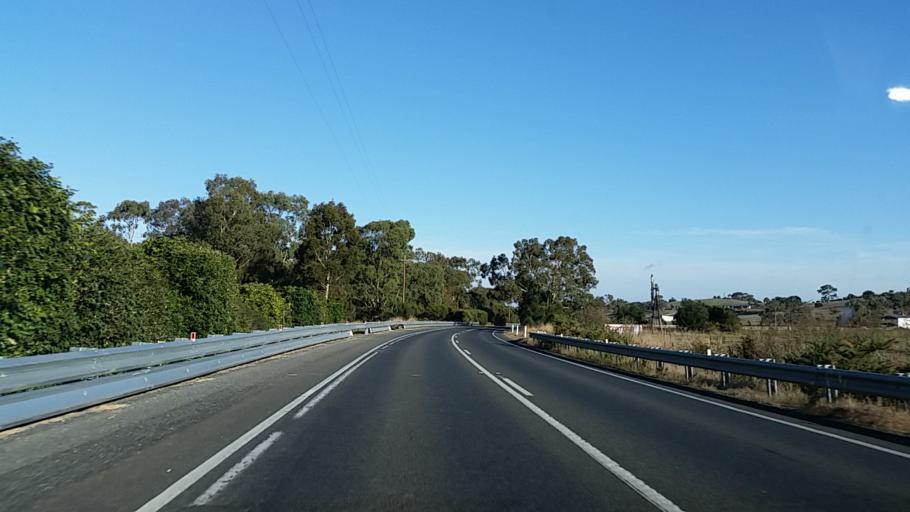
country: AU
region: South Australia
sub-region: Alexandrina
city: Strathalbyn
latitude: -35.2100
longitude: 138.8942
